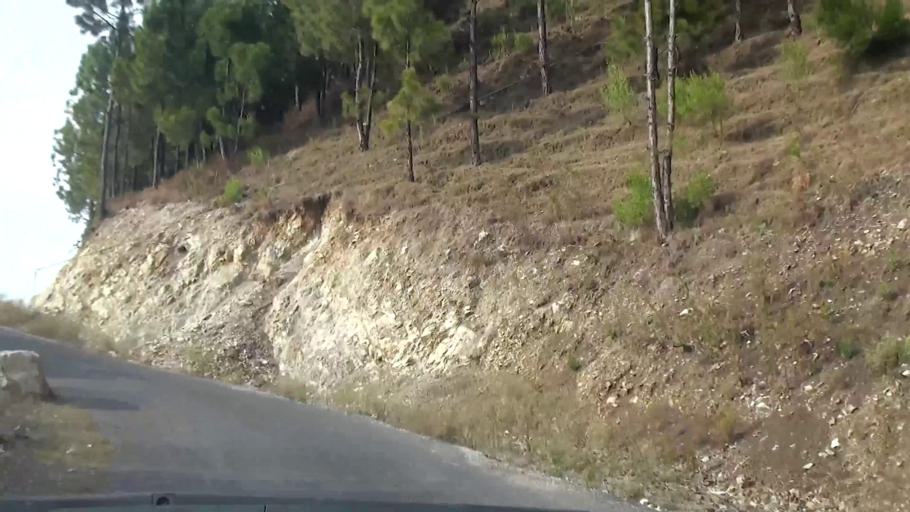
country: PK
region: Azad Kashmir
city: Muzaffarabad
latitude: 34.3632
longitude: 73.5060
